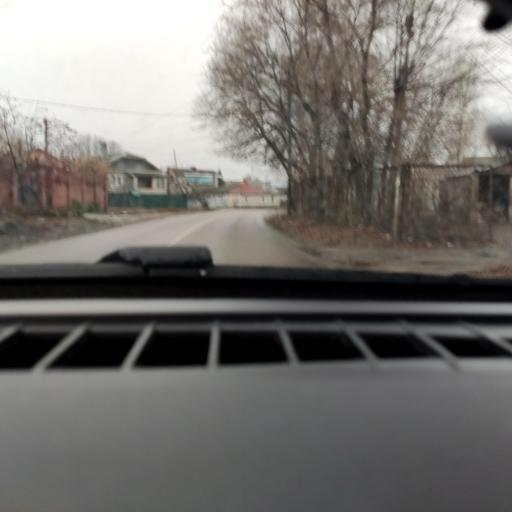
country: RU
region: Voronezj
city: Voronezh
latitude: 51.7284
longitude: 39.2628
